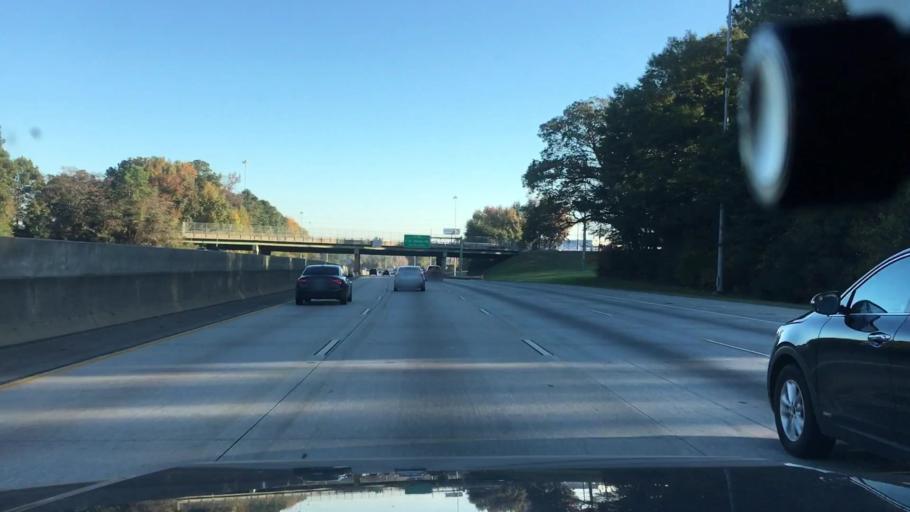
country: US
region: Georgia
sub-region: Fulton County
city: Union City
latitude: 33.5656
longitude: -84.5351
